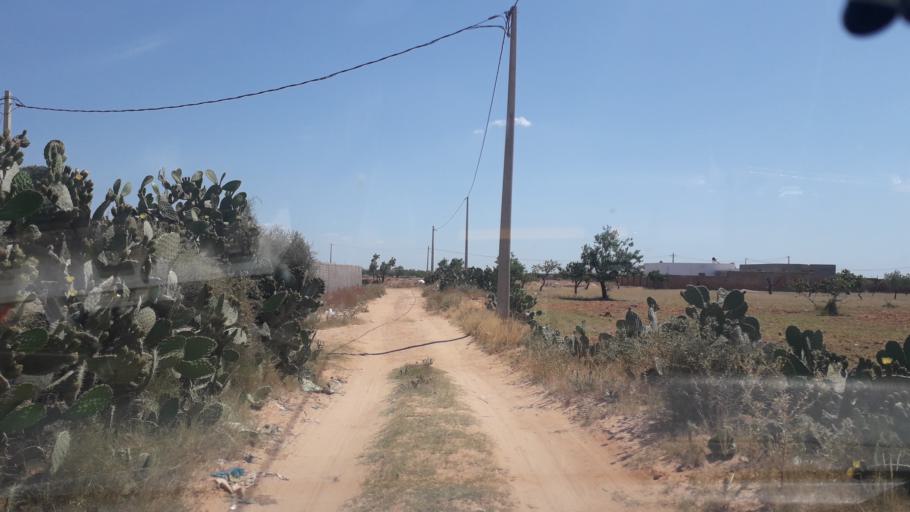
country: TN
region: Safaqis
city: Al Qarmadah
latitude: 34.8347
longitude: 10.7733
